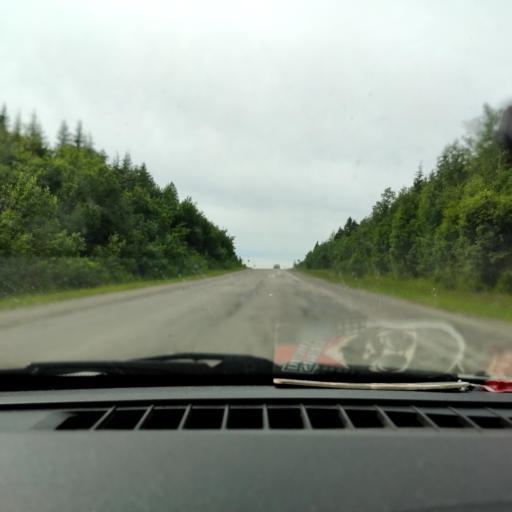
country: RU
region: Perm
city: Chusovoy
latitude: 58.3743
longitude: 57.9678
